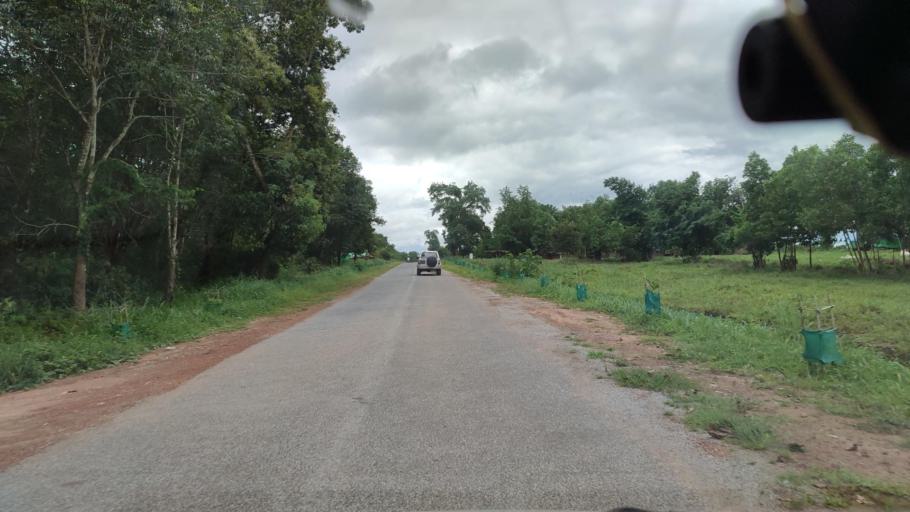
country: MM
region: Bago
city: Thanatpin
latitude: 17.2478
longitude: 96.3295
